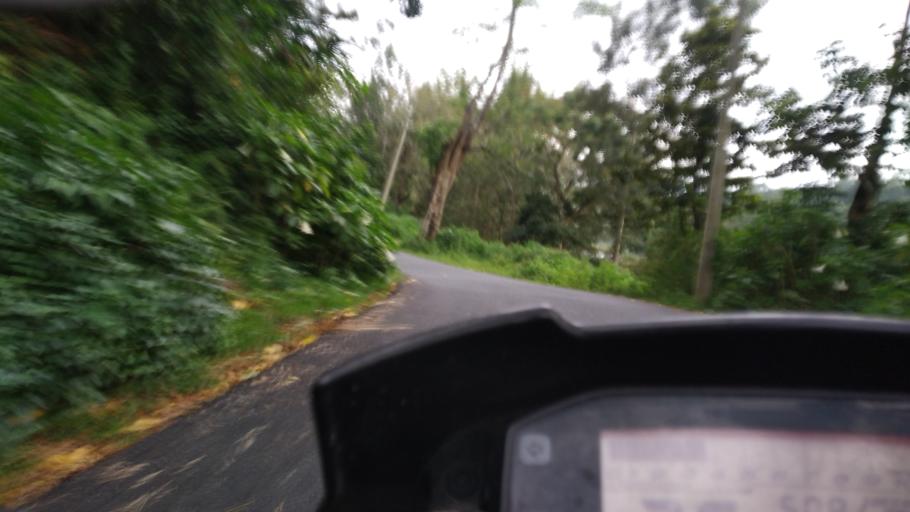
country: IN
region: Tamil Nadu
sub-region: Theni
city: Bodinayakkanur
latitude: 10.0316
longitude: 77.2296
